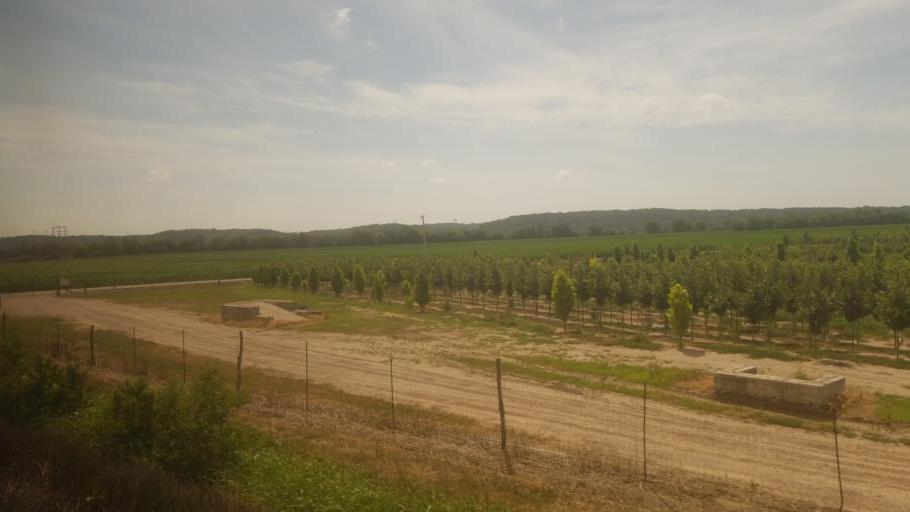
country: US
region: Missouri
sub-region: Jackson County
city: East Independence
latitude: 39.1771
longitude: -94.3262
